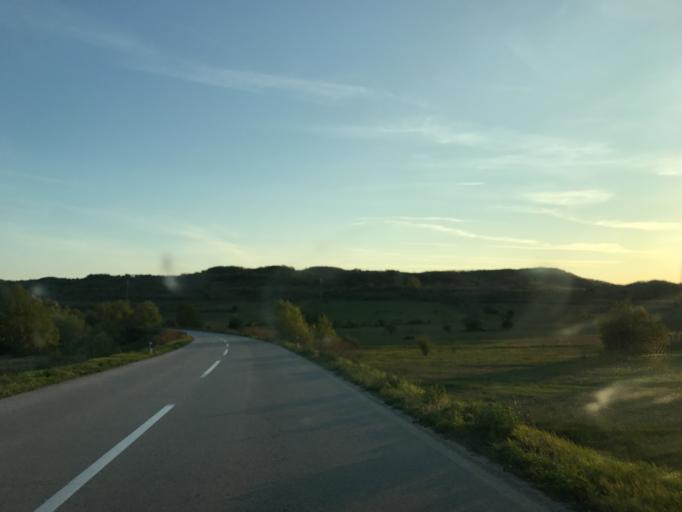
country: RO
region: Mehedinti
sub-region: Comuna Gogosu
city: Ostrovu Mare
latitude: 44.4003
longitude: 22.4675
